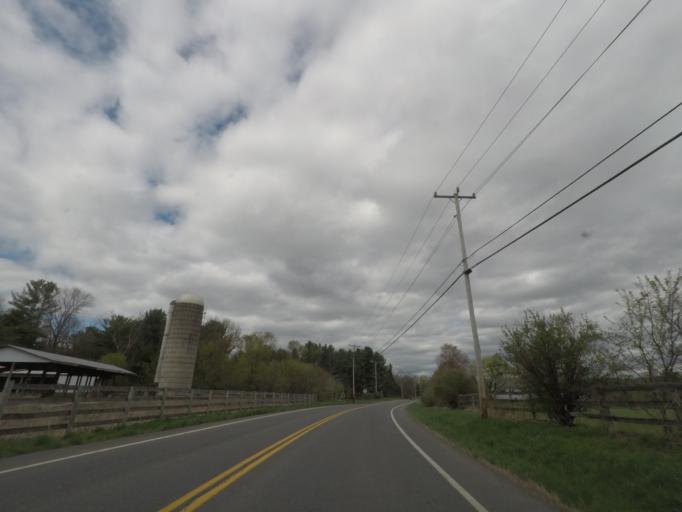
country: US
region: New York
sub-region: Columbia County
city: Philmont
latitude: 42.2787
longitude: -73.6600
